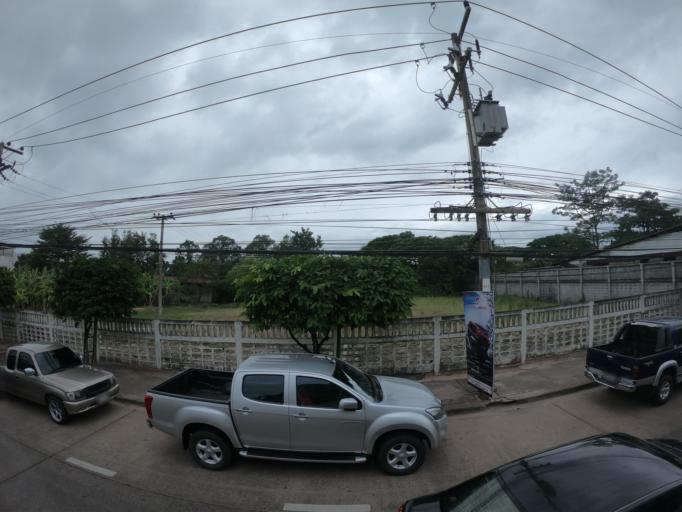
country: TH
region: Roi Et
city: Roi Et
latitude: 16.0526
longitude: 103.6416
